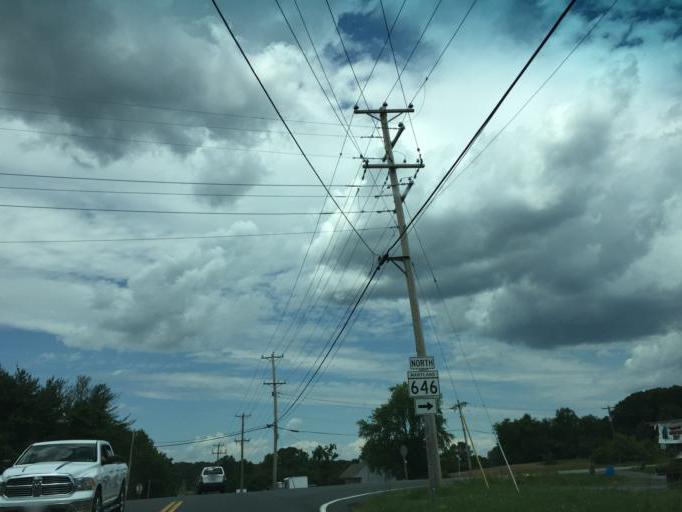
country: US
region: Maryland
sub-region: Harford County
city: Bel Air North
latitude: 39.6516
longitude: -76.3355
